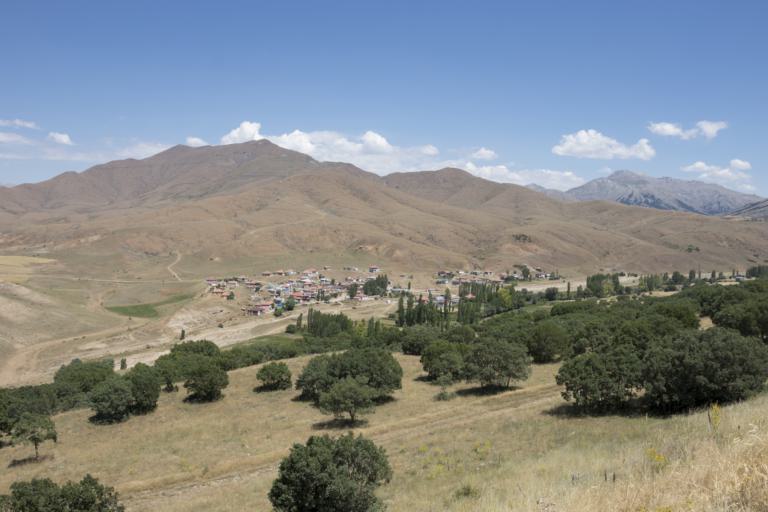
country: TR
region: Kayseri
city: Toklar
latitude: 38.3766
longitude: 35.9983
